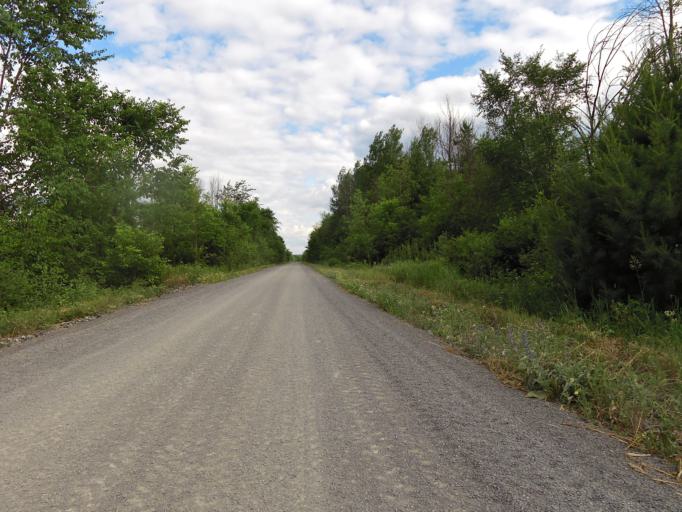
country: CA
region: Ontario
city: Arnprior
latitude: 45.2905
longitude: -76.2550
